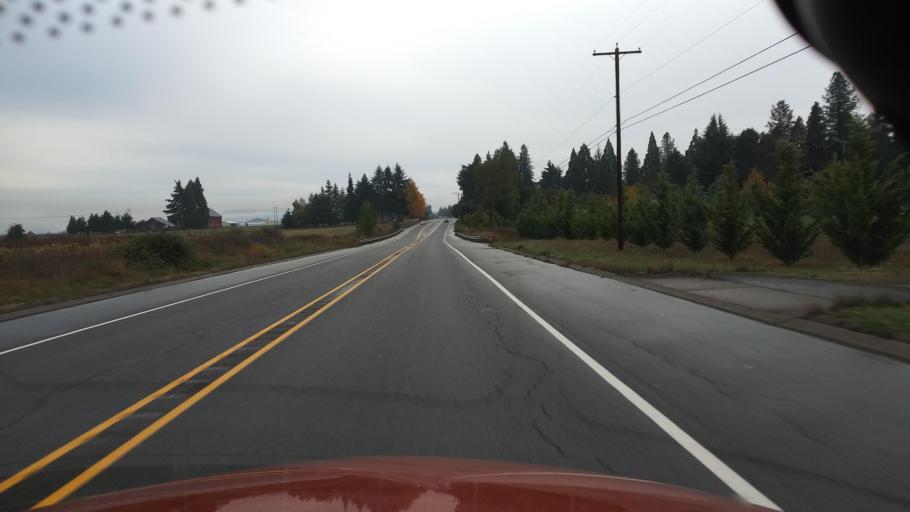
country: US
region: Oregon
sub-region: Washington County
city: Cornelius
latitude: 45.5371
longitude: -123.0598
